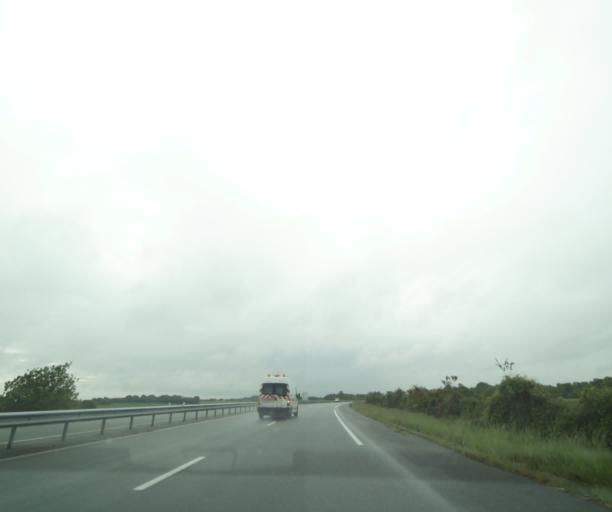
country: FR
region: Poitou-Charentes
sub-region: Departement de la Charente-Maritime
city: Nieul-les-Saintes
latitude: 45.7043
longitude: -0.7603
